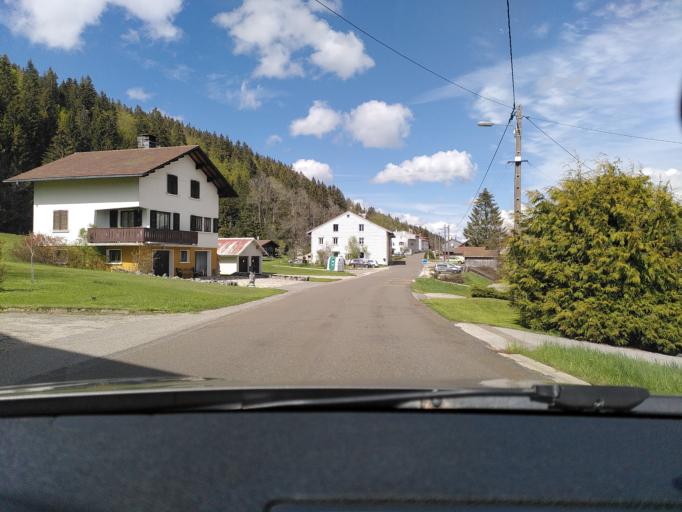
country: FR
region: Franche-Comte
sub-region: Departement du Jura
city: Les Rousses
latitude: 46.5239
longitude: 6.1126
